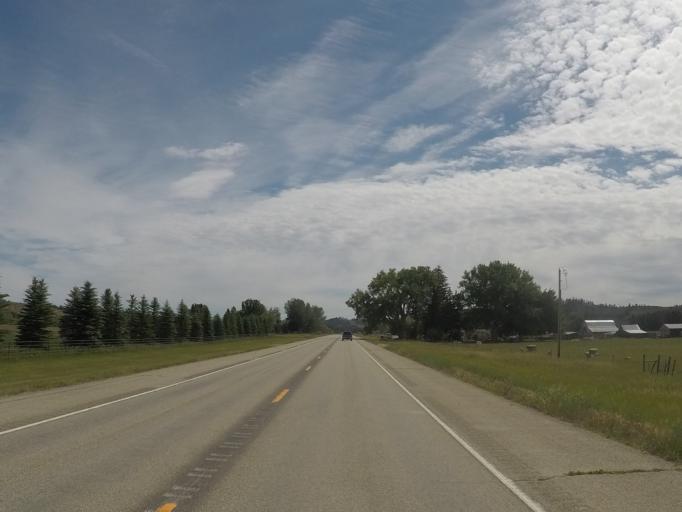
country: US
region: Montana
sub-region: Stillwater County
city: Columbus
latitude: 45.4698
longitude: -109.0222
